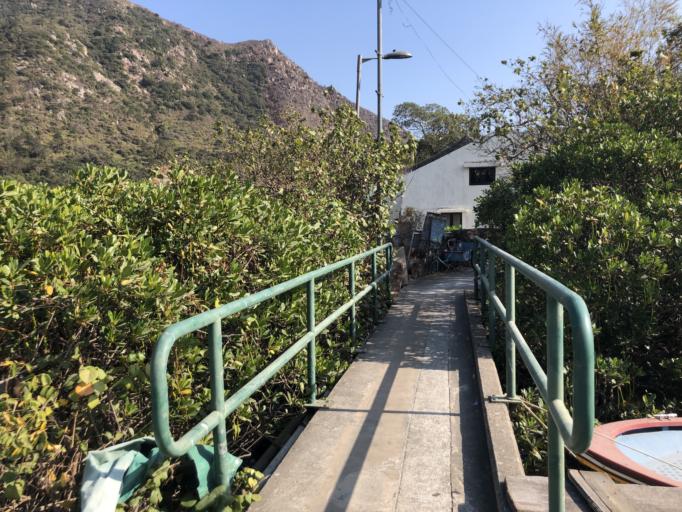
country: HK
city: Tai O
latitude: 22.2547
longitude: 113.8671
